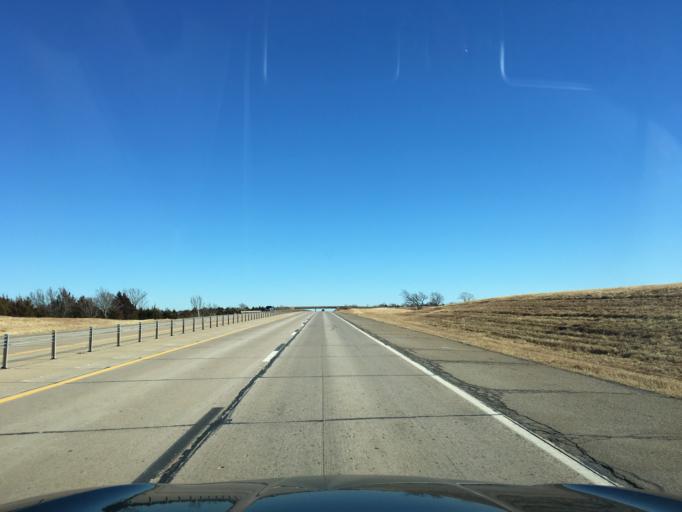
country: US
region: Oklahoma
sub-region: Pawnee County
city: Pawnee
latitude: 36.2250
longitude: -96.8442
